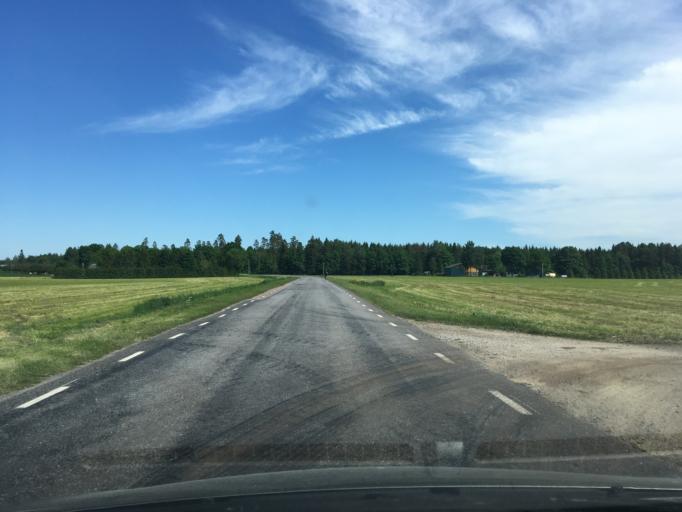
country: EE
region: Raplamaa
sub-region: Rapla vald
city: Rapla
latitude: 59.0572
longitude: 24.9068
